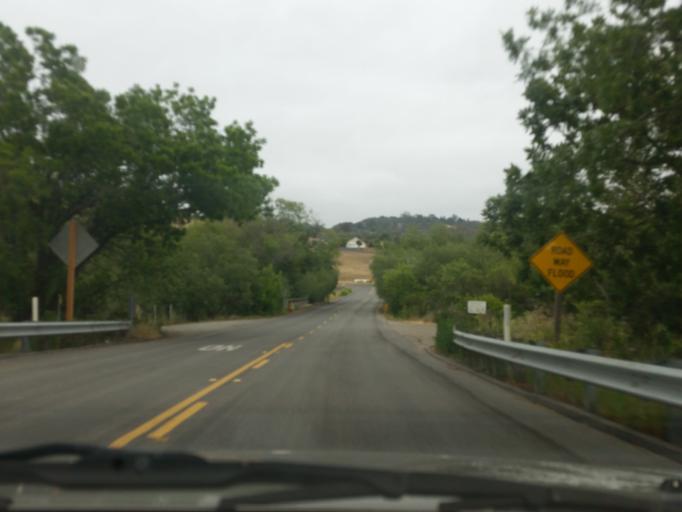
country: US
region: California
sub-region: San Luis Obispo County
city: Avila Beach
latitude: 35.1960
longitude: -120.6980
